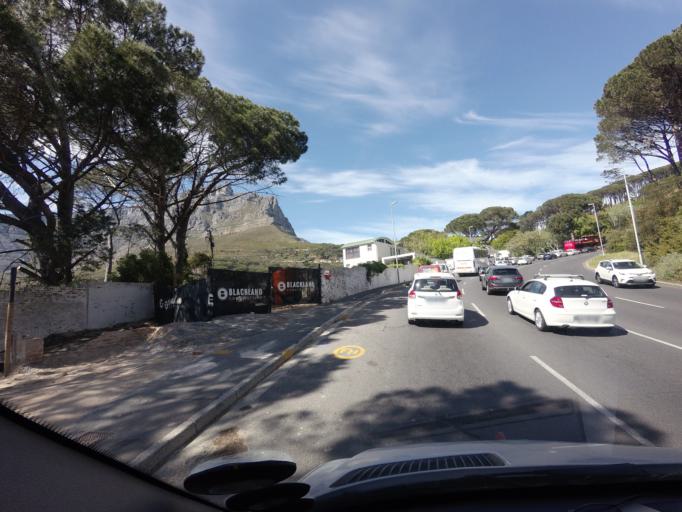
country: ZA
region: Western Cape
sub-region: City of Cape Town
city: Cape Town
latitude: -33.9386
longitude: 18.3983
